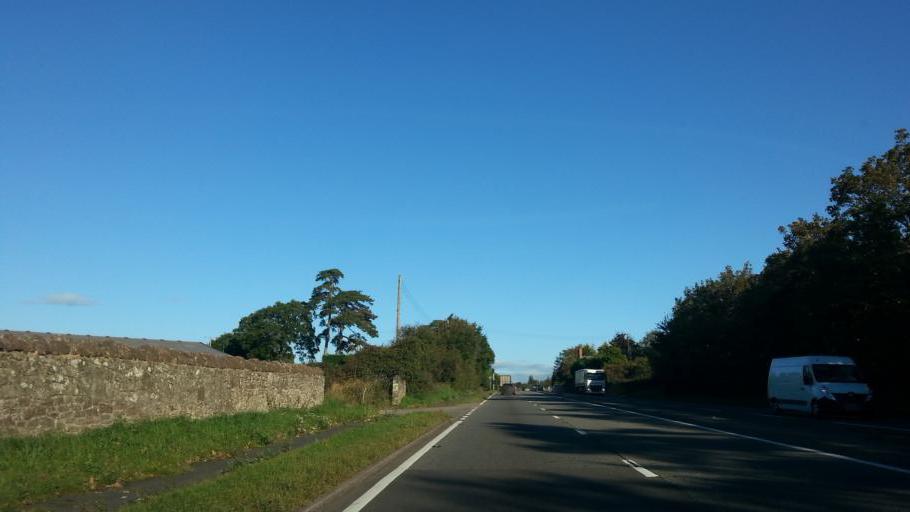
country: GB
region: England
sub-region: Herefordshire
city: Marstow
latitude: 51.8818
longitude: -2.6320
